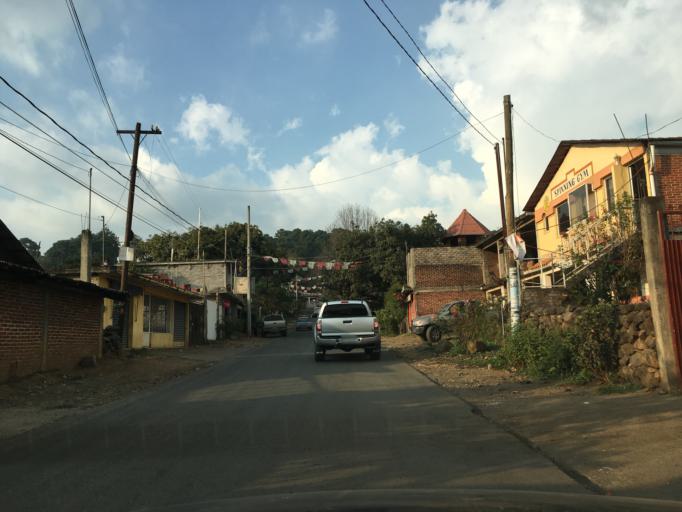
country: MX
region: Michoacan
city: Tingambato
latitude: 19.4498
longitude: -101.8874
